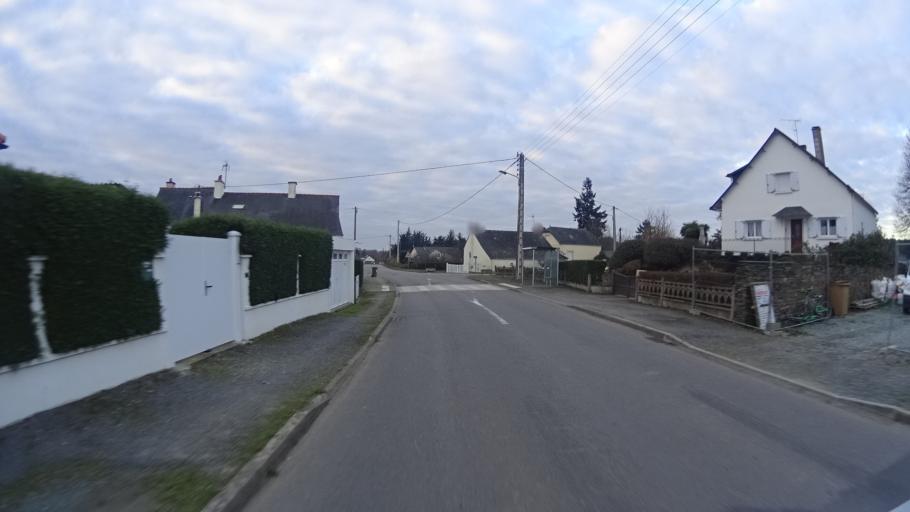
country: FR
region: Brittany
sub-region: Departement d'Ille-et-Vilaine
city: Langon
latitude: 47.6941
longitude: -1.8680
